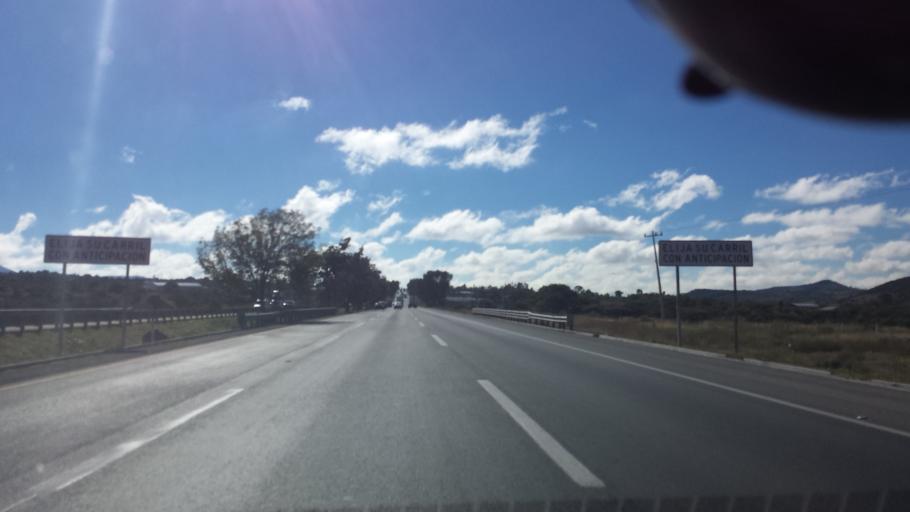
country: MX
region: Mexico
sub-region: Aculco
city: El Colorado
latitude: 20.1808
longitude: -99.7658
